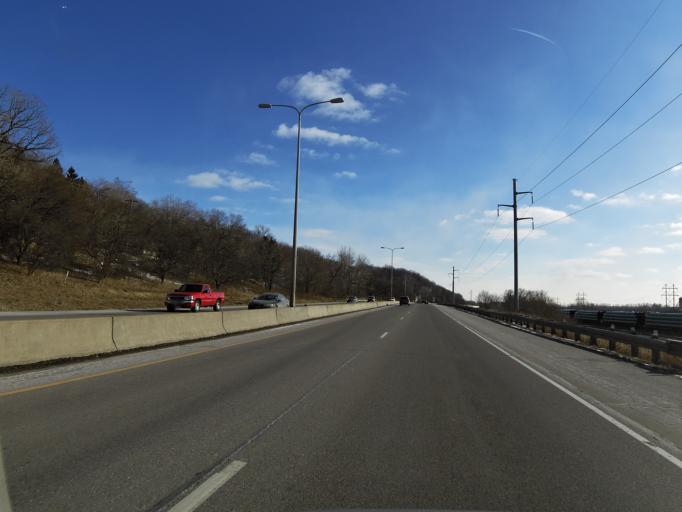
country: US
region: Minnesota
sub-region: Dakota County
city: South Saint Paul
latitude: 44.9206
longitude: -93.0170
